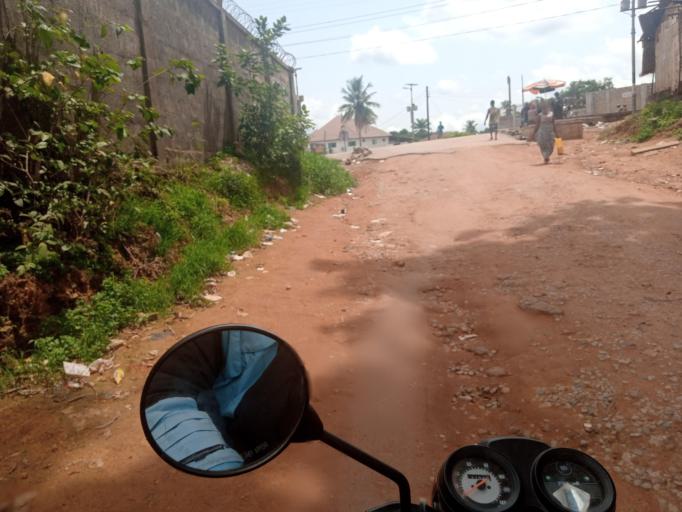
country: SL
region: Southern Province
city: Bo
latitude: 7.9594
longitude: -11.7395
